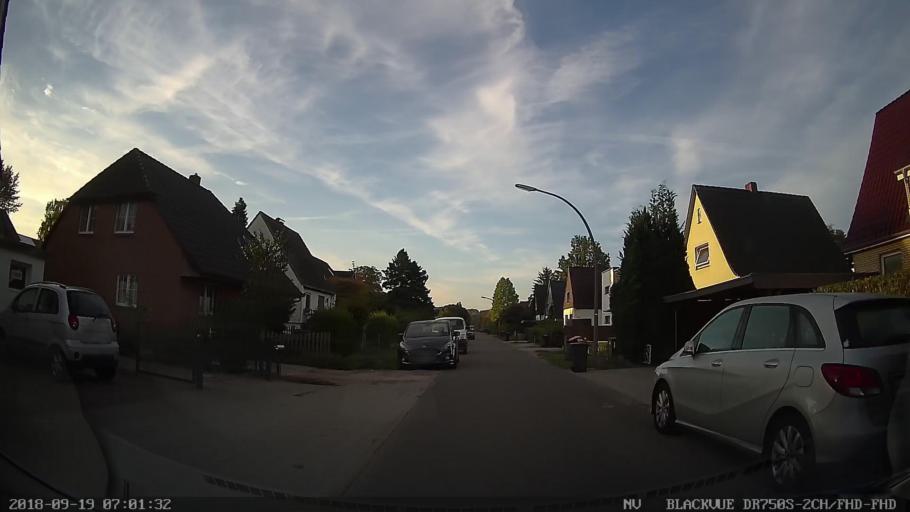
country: DE
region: Hamburg
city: Eidelstedt
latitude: 53.6291
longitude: 9.8987
